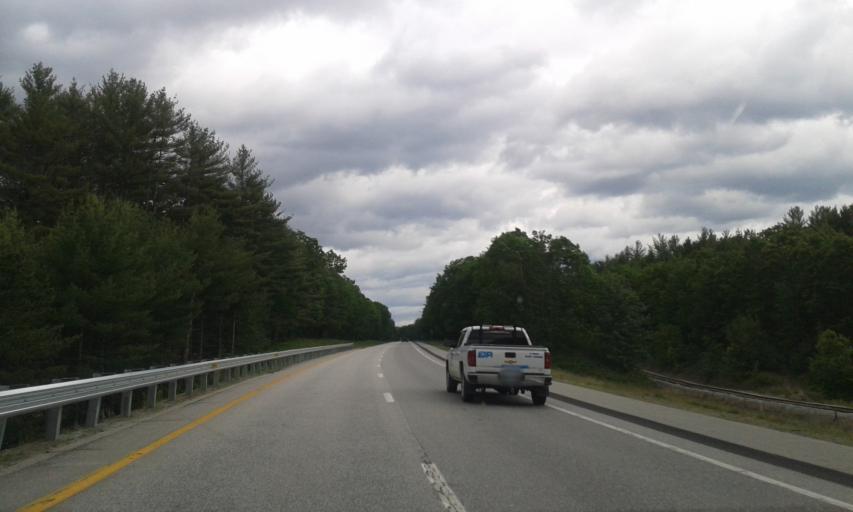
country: US
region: New Hampshire
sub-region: Merrimack County
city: Canterbury
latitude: 43.3147
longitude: -71.5885
